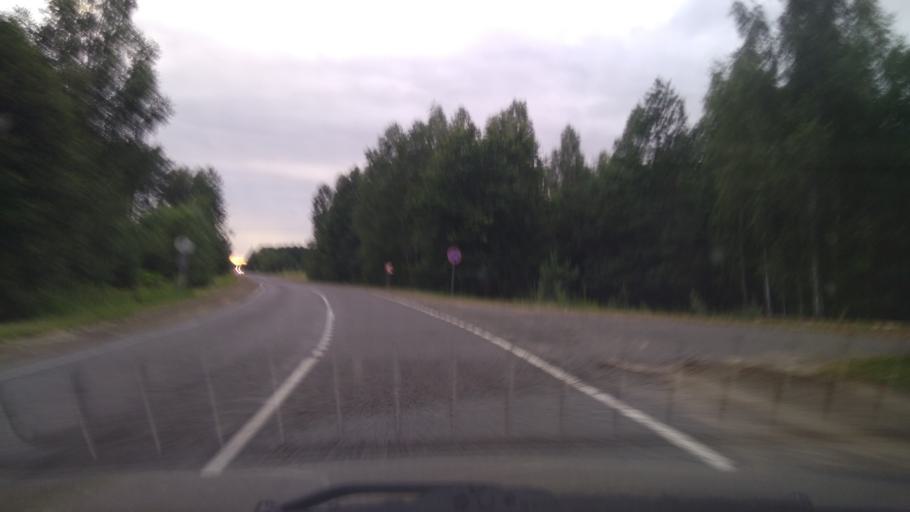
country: BY
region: Brest
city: Byaroza
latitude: 52.4131
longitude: 24.9904
